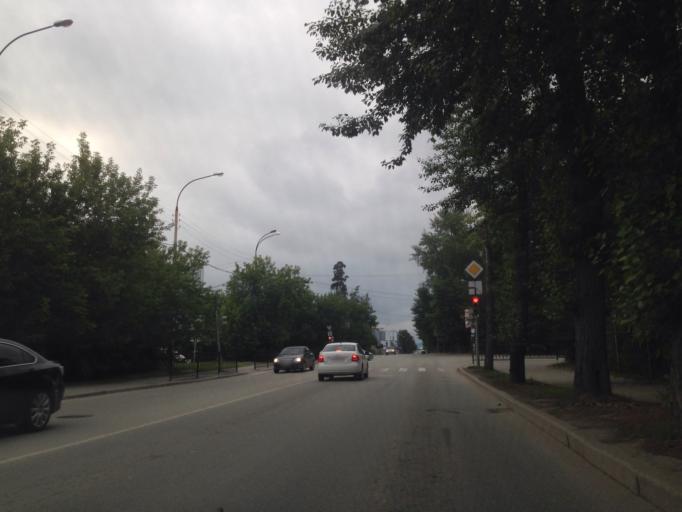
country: RU
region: Sverdlovsk
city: Yekaterinburg
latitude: 56.8342
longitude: 60.6944
